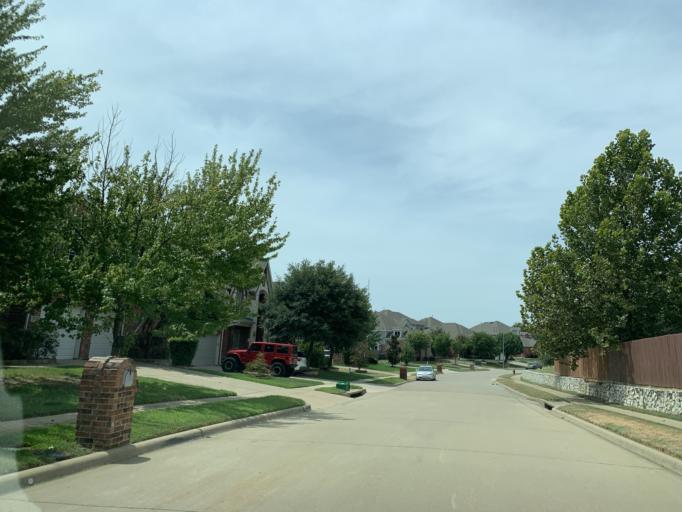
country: US
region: Texas
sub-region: Dallas County
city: Cedar Hill
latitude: 32.6524
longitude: -97.0008
